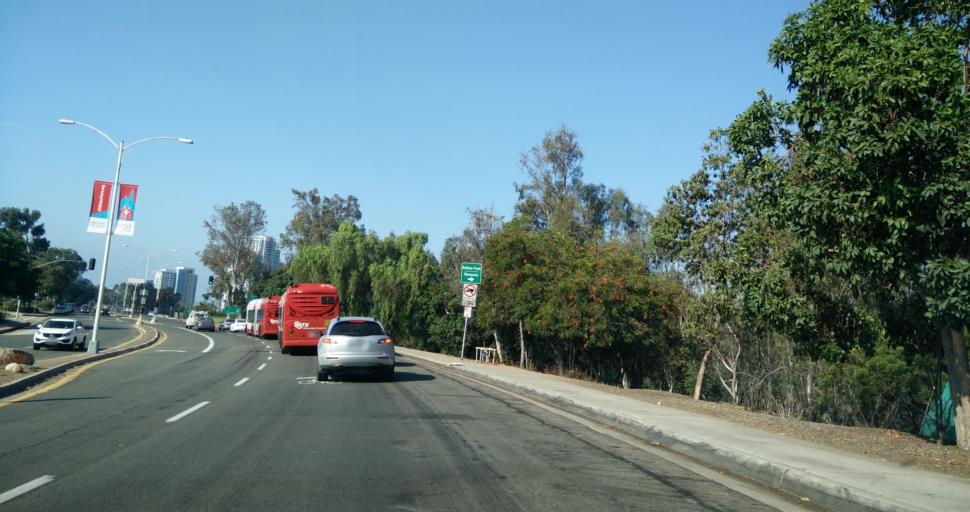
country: US
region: California
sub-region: San Diego County
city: San Diego
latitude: 32.7265
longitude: -117.1500
